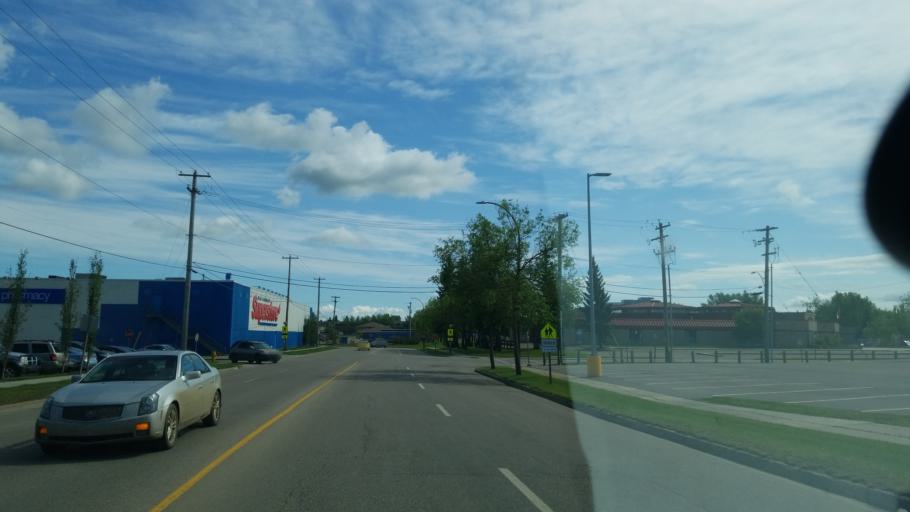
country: CA
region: Saskatchewan
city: Lloydminster
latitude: 53.2767
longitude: -110.0099
